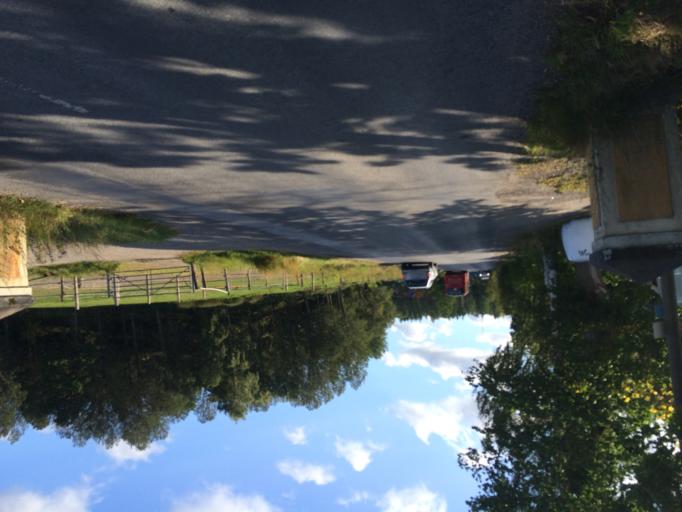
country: SE
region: Stockholm
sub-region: Haninge Kommun
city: Handen
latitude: 59.2198
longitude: 18.0815
